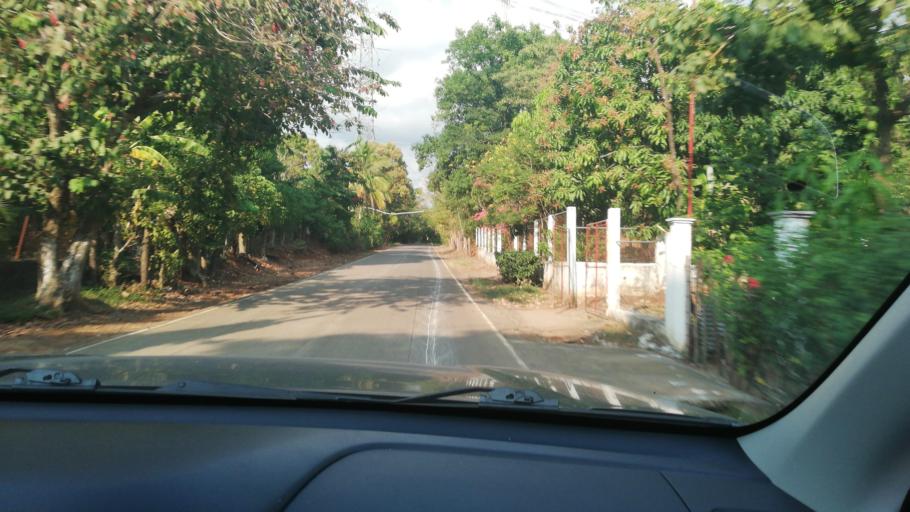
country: GT
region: Quetzaltenango
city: Genova
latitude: 14.5647
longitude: -91.8541
